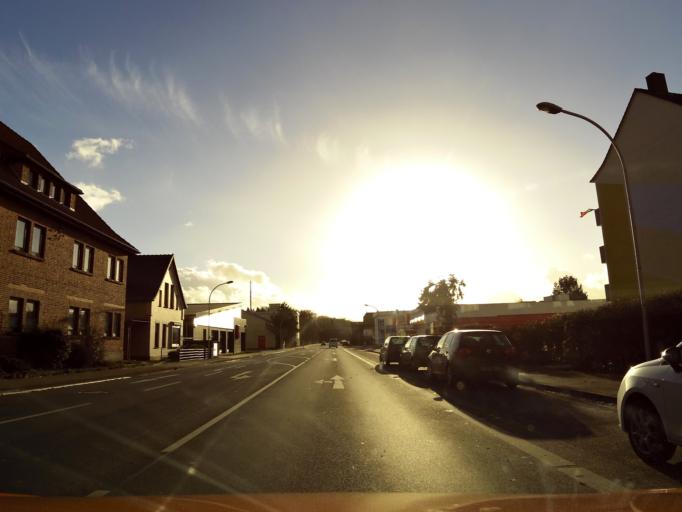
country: DE
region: Lower Saxony
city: Verden
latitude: 52.9374
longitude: 9.2313
